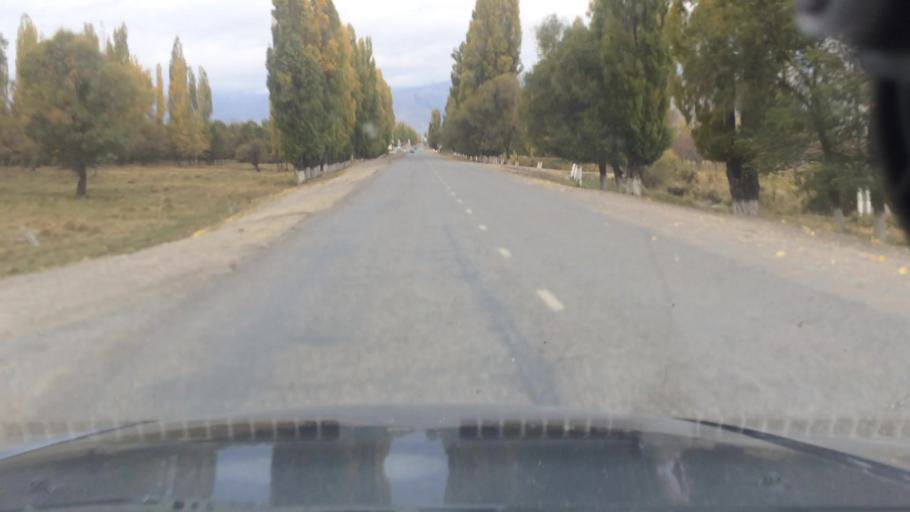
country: KG
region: Ysyk-Koel
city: Tyup
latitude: 42.7353
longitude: 78.3511
